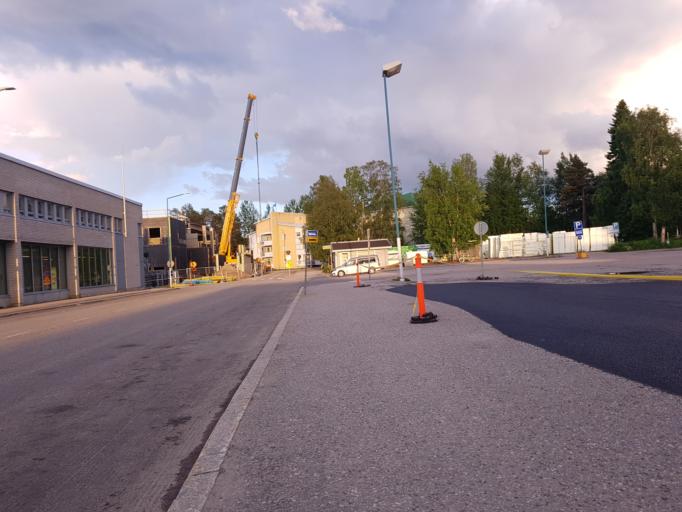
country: FI
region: Kainuu
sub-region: Kajaani
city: Kajaani
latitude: 64.2223
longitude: 27.7297
